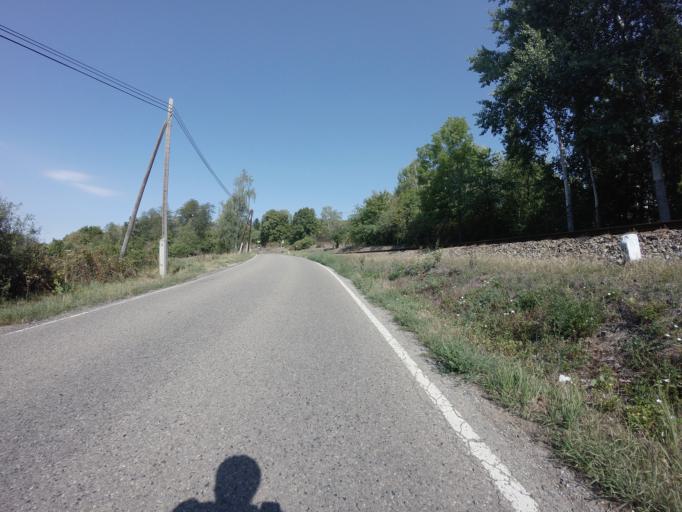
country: CZ
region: Central Bohemia
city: Kamenny Privoz
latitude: 49.8607
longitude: 14.5411
